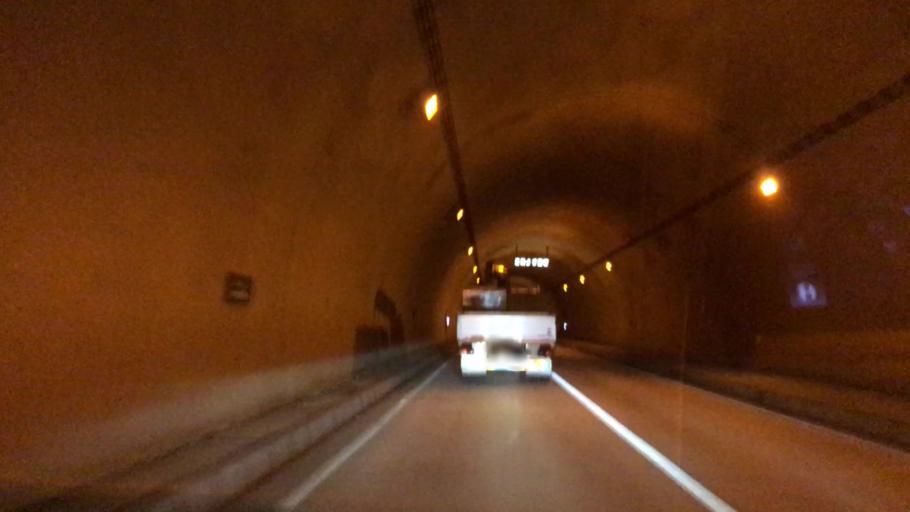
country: JP
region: Hokkaido
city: Iwanai
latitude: 43.1205
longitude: 140.4469
